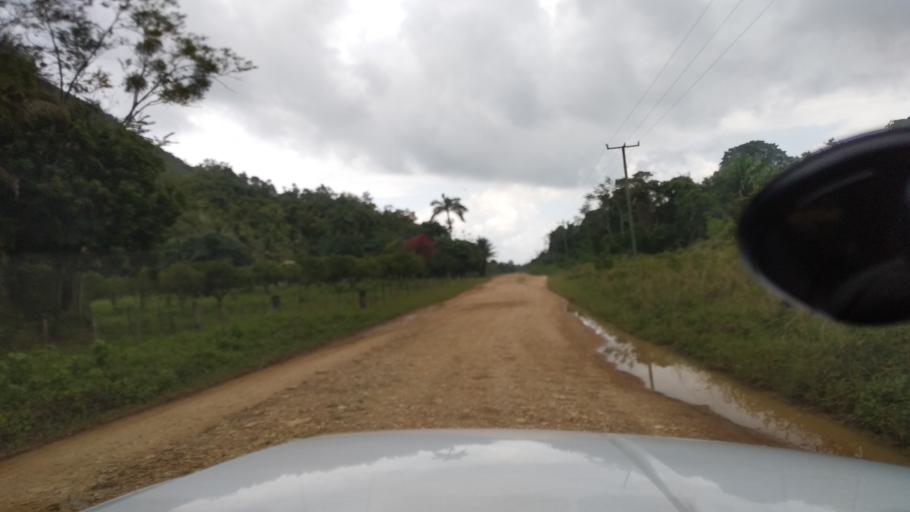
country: BZ
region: Toledo
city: Punta Gorda
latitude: 16.2116
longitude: -89.0206
